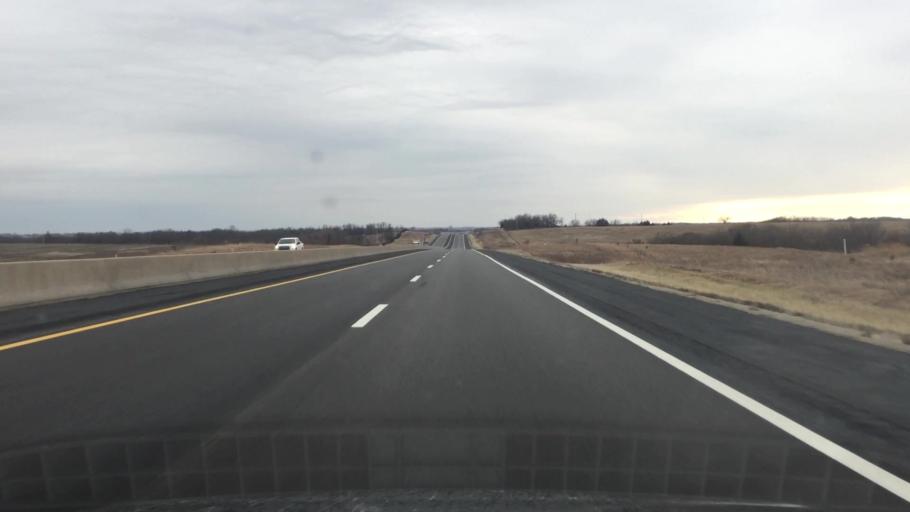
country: US
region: Kansas
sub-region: Shawnee County
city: Auburn
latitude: 38.7886
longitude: -95.9135
